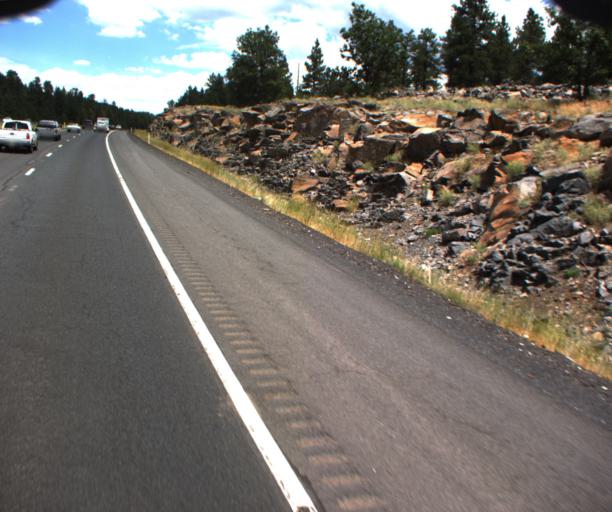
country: US
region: Arizona
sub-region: Coconino County
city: Mountainaire
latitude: 34.9712
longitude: -111.6843
